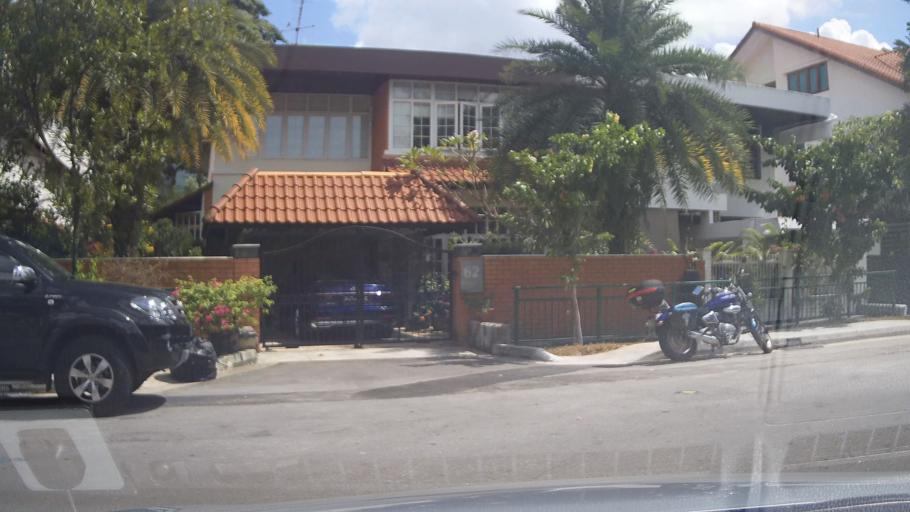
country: SG
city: Singapore
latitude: 1.3233
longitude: 103.7560
